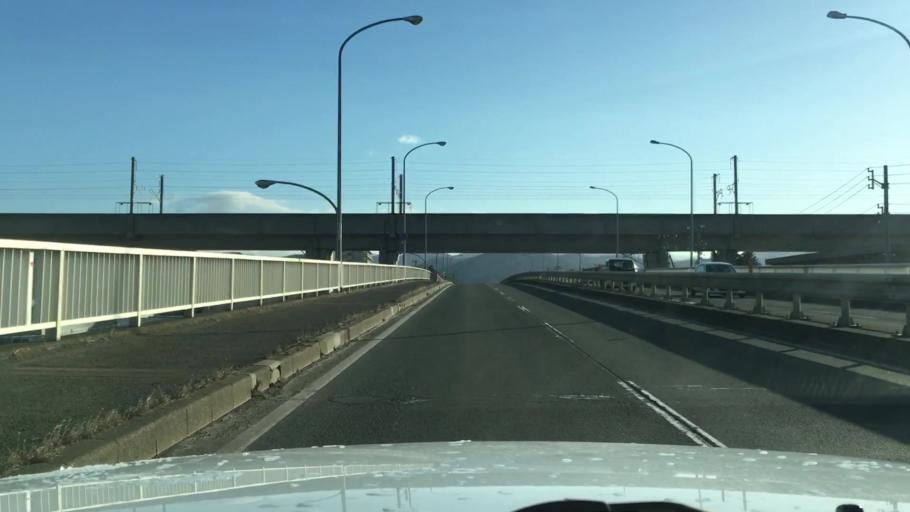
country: JP
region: Iwate
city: Morioka-shi
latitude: 39.6571
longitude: 141.1457
